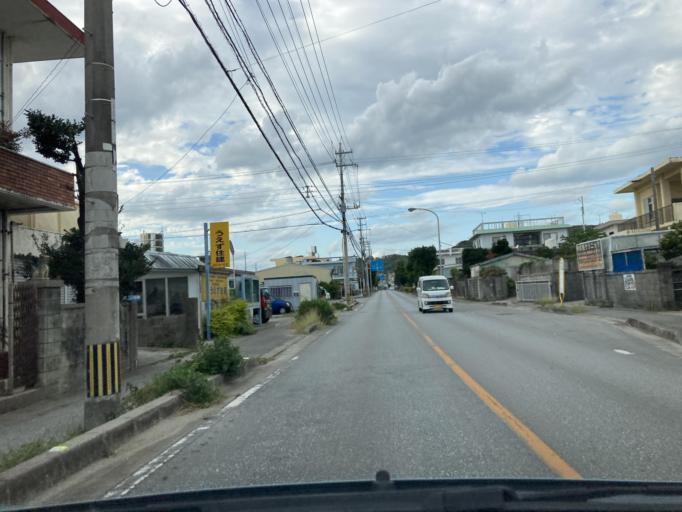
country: JP
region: Okinawa
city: Katsuren-haebaru
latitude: 26.3424
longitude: 127.8694
